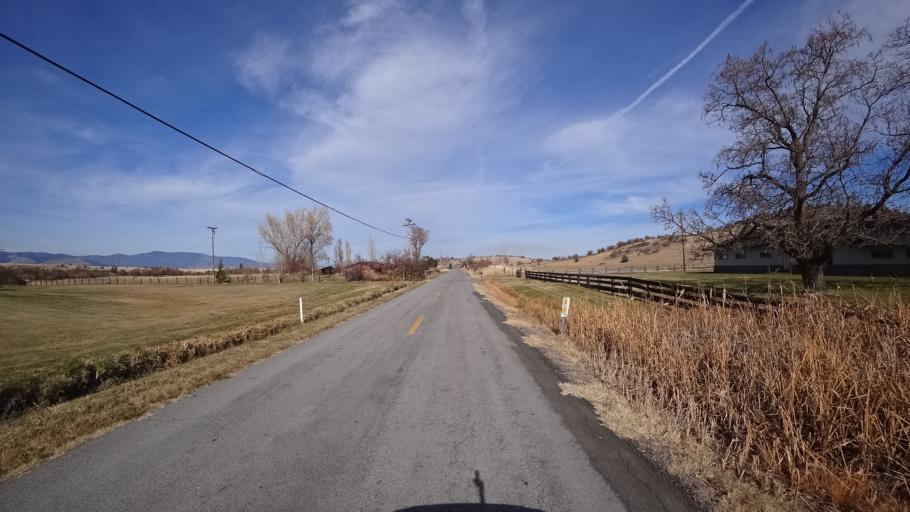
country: US
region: California
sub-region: Siskiyou County
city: Weed
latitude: 41.4646
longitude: -122.4342
